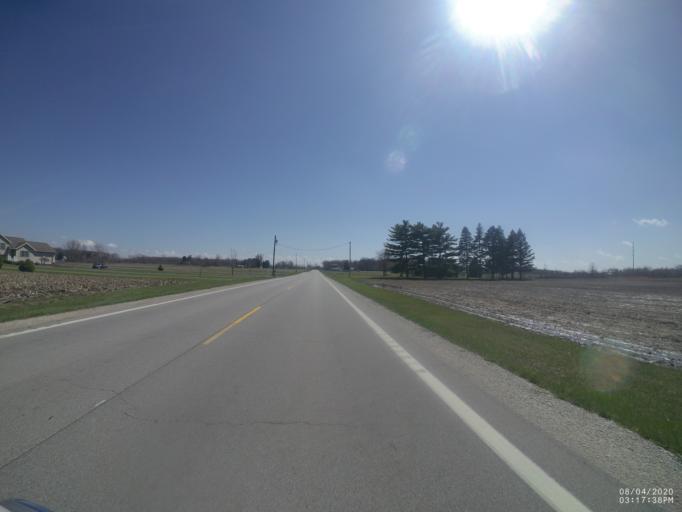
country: US
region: Ohio
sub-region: Sandusky County
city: Stony Prairie
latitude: 41.2720
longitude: -83.2353
